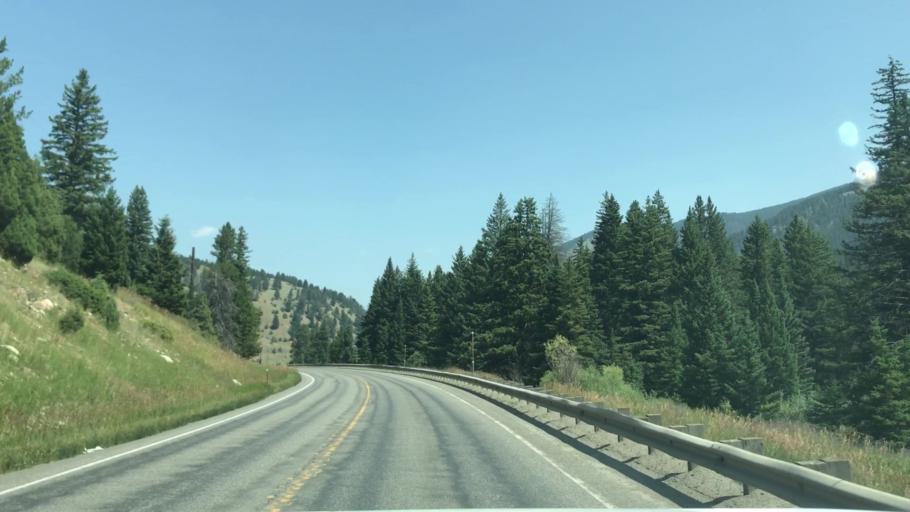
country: US
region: Montana
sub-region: Gallatin County
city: Big Sky
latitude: 45.2714
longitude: -111.2430
